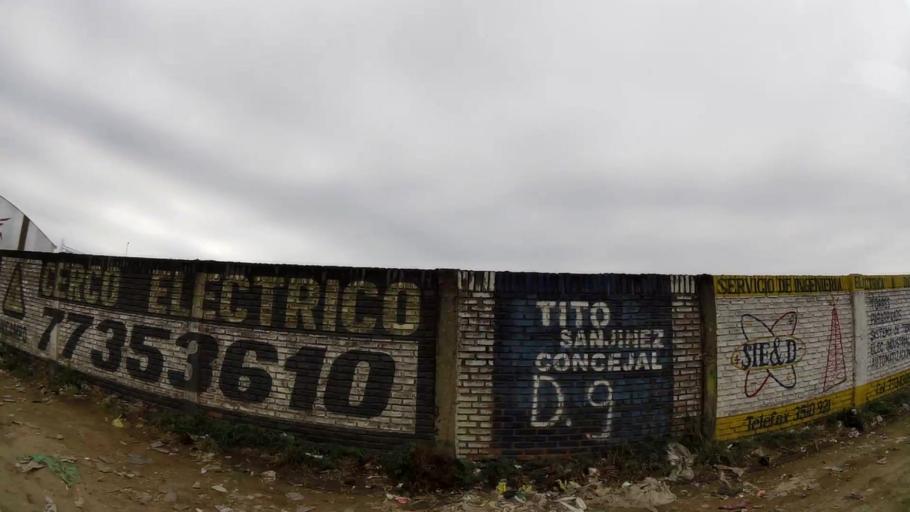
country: BO
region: Santa Cruz
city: Santa Cruz de la Sierra
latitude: -17.8230
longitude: -63.1643
